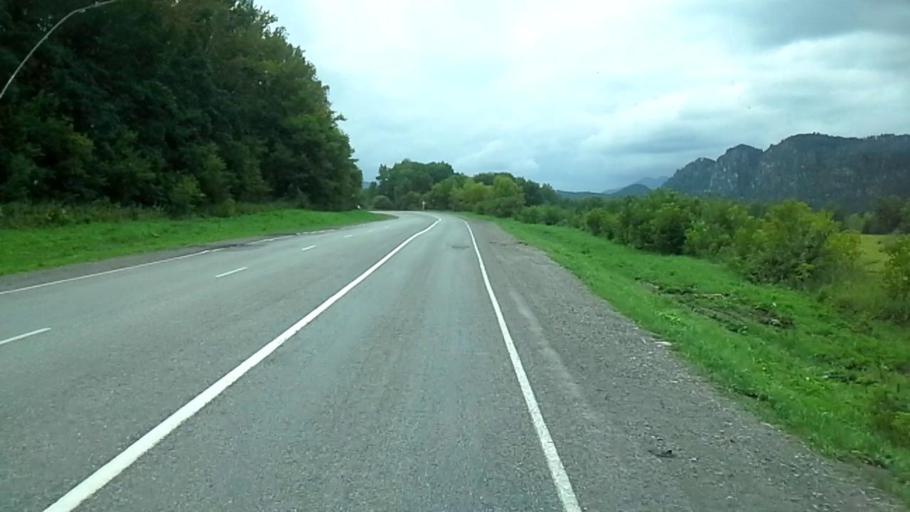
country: RU
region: Altay
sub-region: Mayminskiy Rayon
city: Manzherok
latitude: 51.8635
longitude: 85.7630
